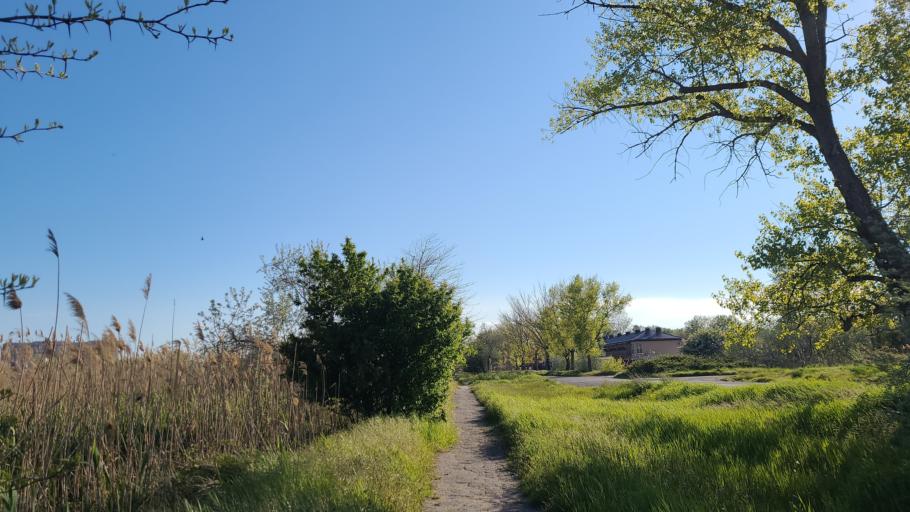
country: RU
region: Krasnodarskiy
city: Tsibanobalka
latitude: 44.9486
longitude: 37.3094
